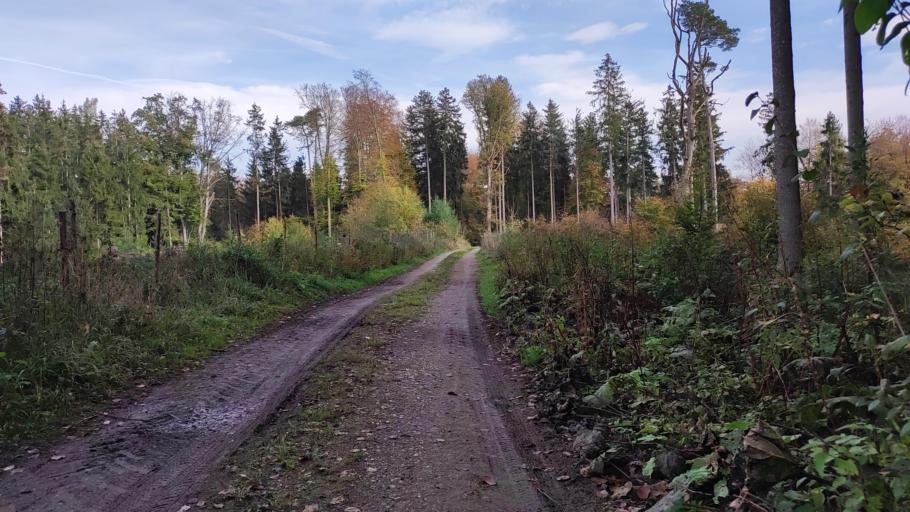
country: DE
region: Bavaria
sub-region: Swabia
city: Ziemetshausen
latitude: 48.2906
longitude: 10.5629
